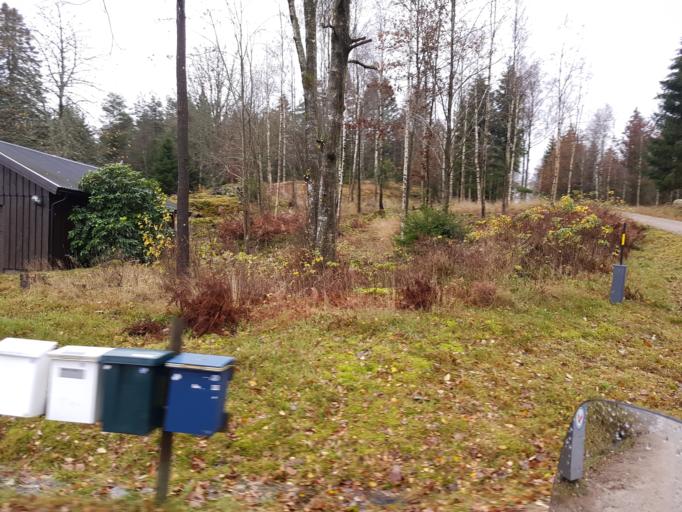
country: SE
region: Vaestra Goetaland
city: Svanesund
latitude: 58.1845
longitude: 11.8220
